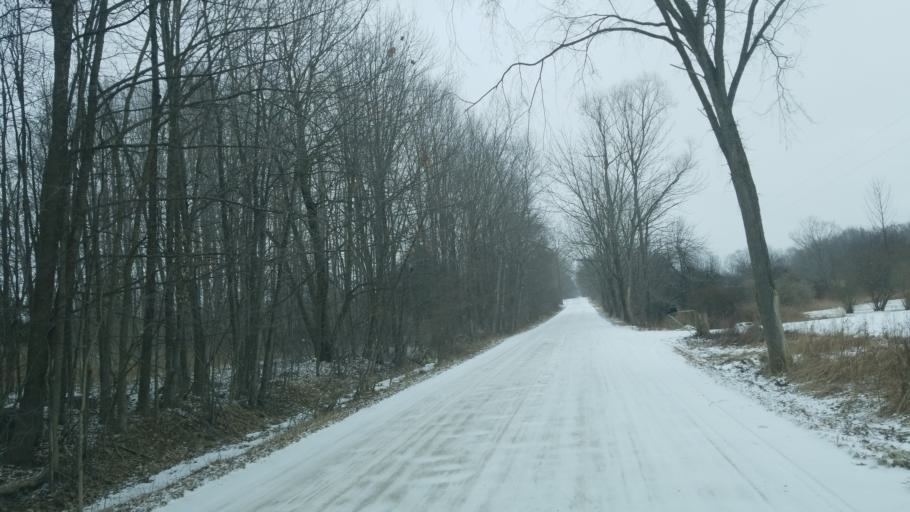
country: US
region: Michigan
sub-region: Osceola County
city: Evart
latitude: 44.0159
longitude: -85.2362
